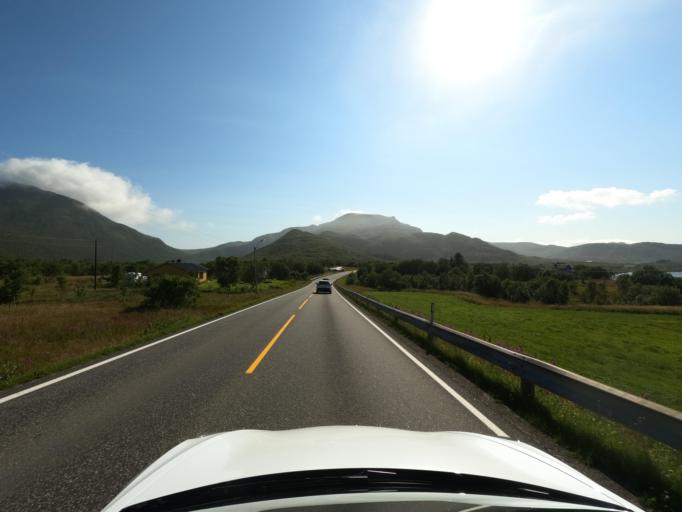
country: NO
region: Nordland
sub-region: Vestvagoy
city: Evjen
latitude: 68.2605
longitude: 14.0452
